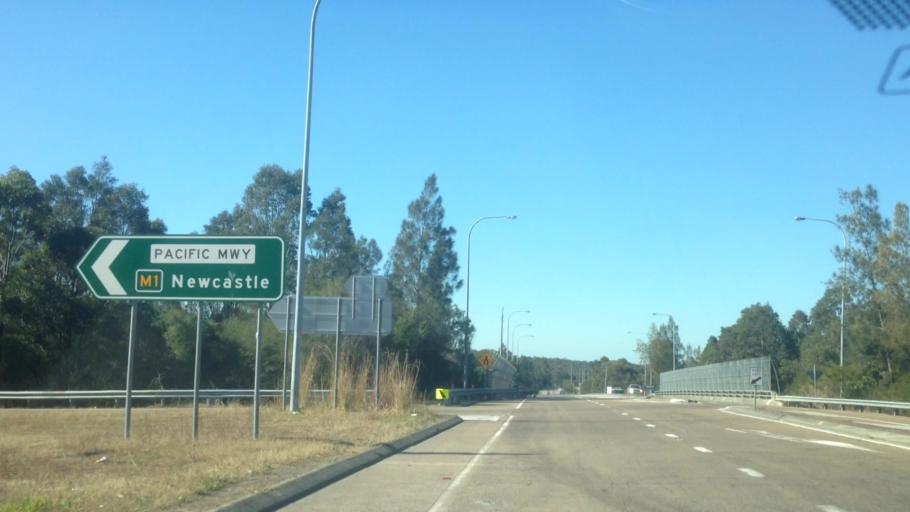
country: AU
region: New South Wales
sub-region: Lake Macquarie Shire
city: Cooranbong
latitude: -33.1190
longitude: 151.4646
